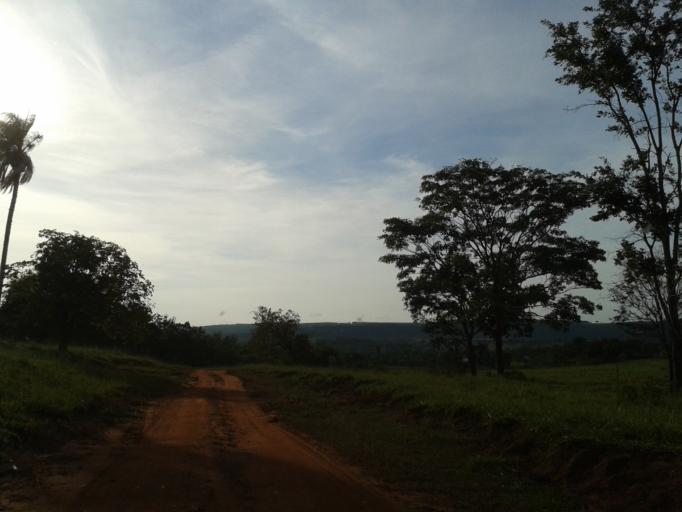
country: BR
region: Minas Gerais
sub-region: Campina Verde
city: Campina Verde
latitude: -19.4931
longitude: -49.6068
